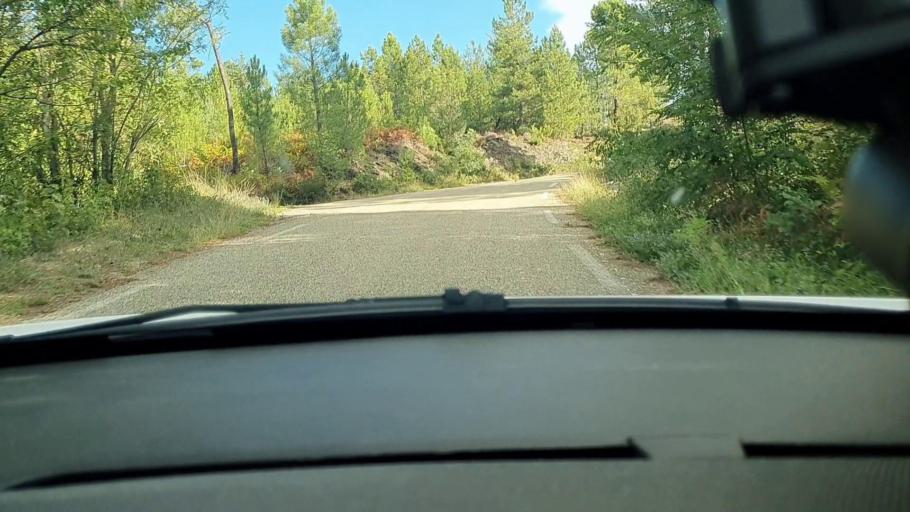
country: FR
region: Languedoc-Roussillon
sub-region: Departement du Gard
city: Besseges
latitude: 44.3481
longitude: 3.9814
